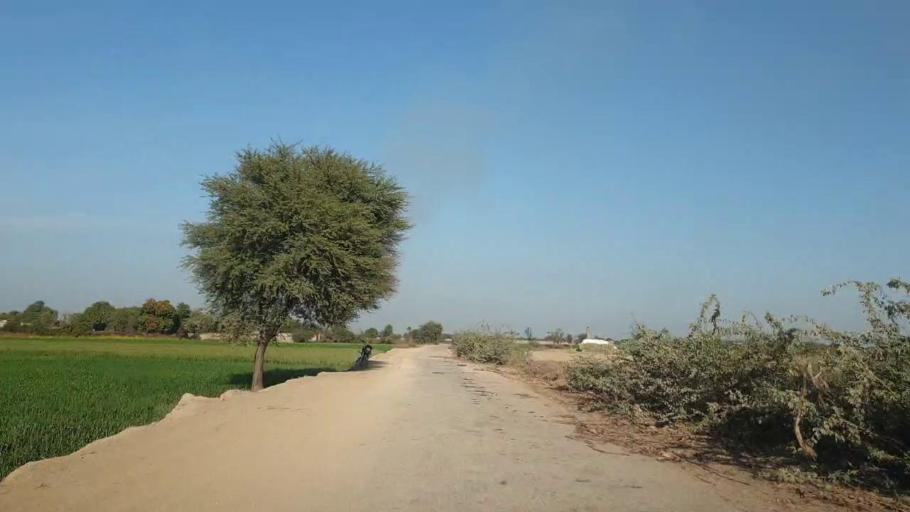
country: PK
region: Sindh
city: Tando Adam
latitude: 25.6995
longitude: 68.6903
